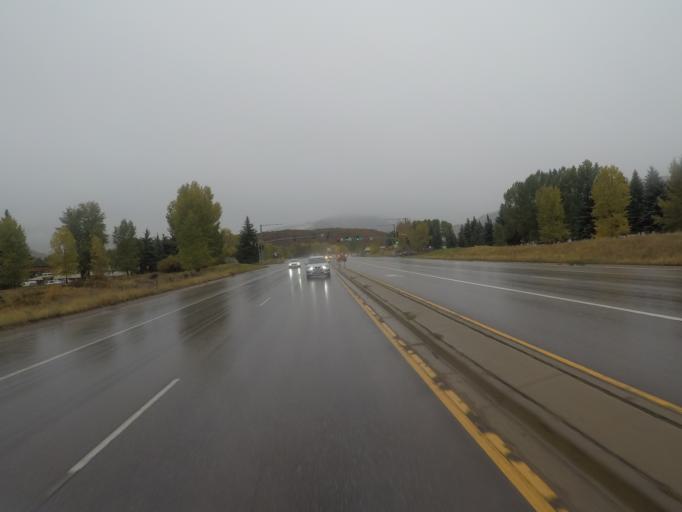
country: US
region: Colorado
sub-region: Pitkin County
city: Aspen
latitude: 39.2214
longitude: -106.8638
